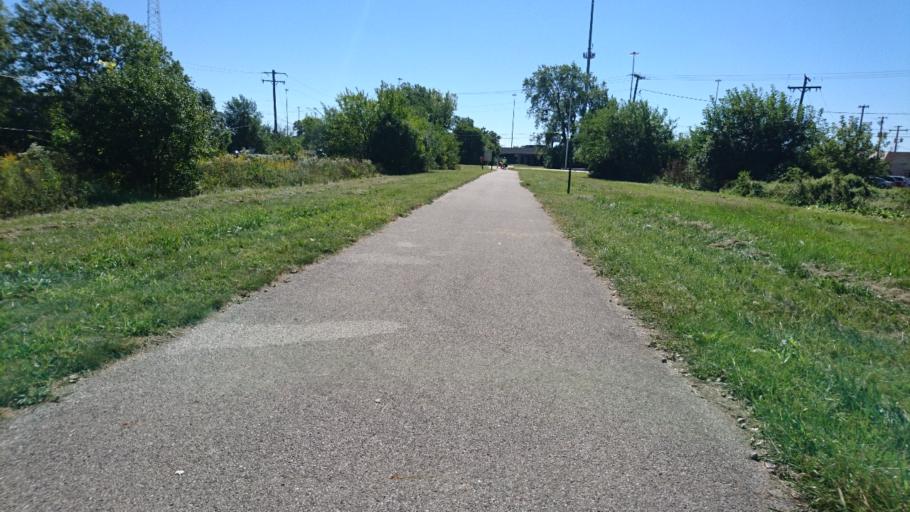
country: US
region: Illinois
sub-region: Cook County
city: Lansing
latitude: 41.5800
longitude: -87.5500
